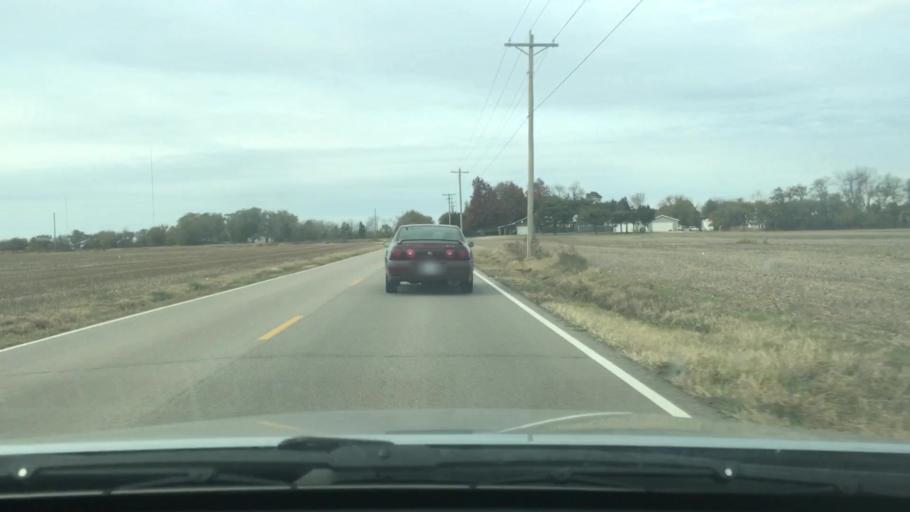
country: US
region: Kansas
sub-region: Sedgwick County
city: Maize
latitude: 37.7495
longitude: -97.4993
